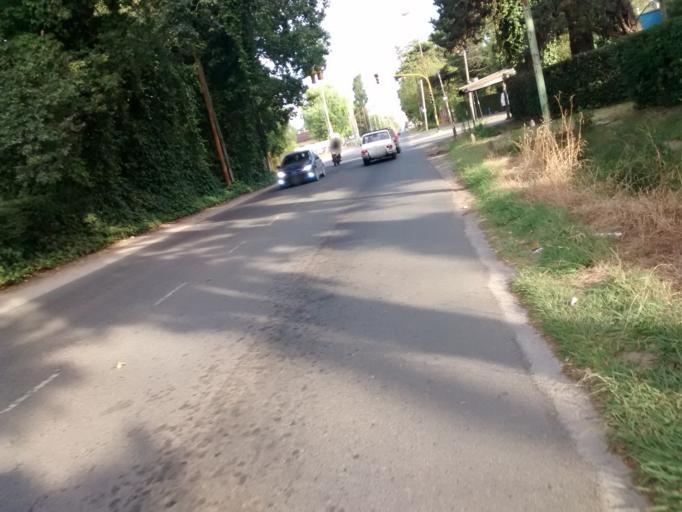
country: AR
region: Buenos Aires
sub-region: Partido de La Plata
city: La Plata
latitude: -34.8640
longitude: -58.1105
